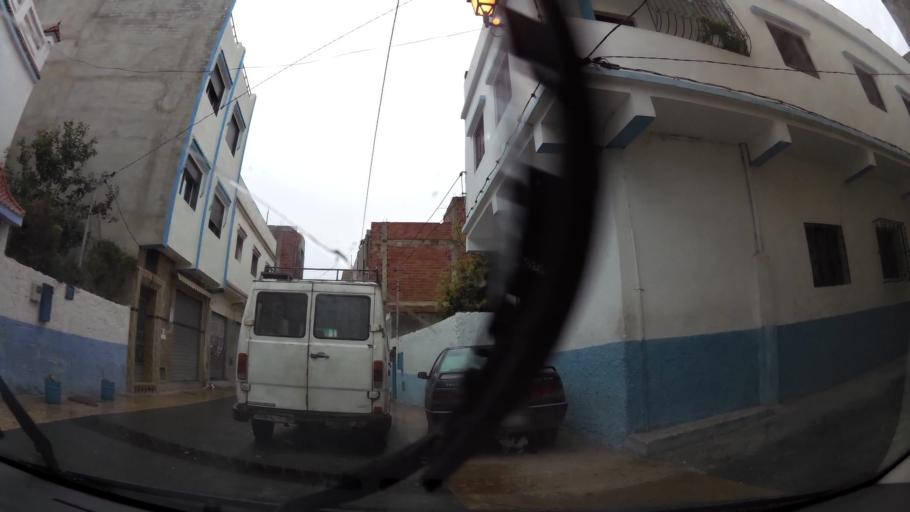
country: MA
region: Tanger-Tetouan
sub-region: Tetouan
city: Martil
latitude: 35.6230
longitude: -5.2812
